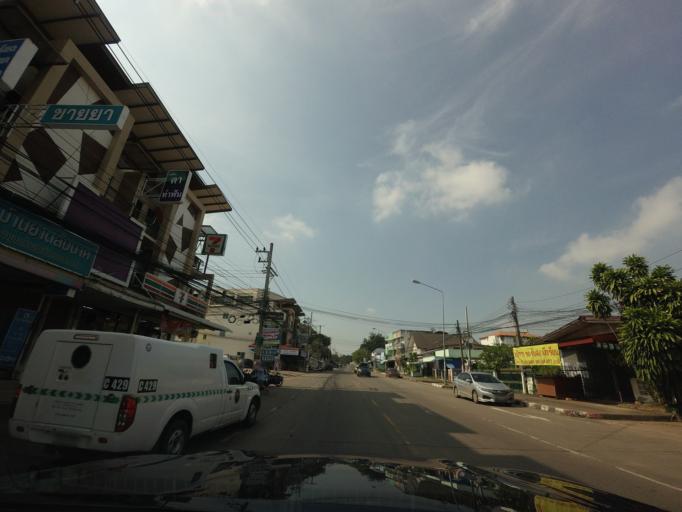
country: TH
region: Khon Kaen
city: Khon Kaen
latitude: 16.4253
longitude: 102.8509
